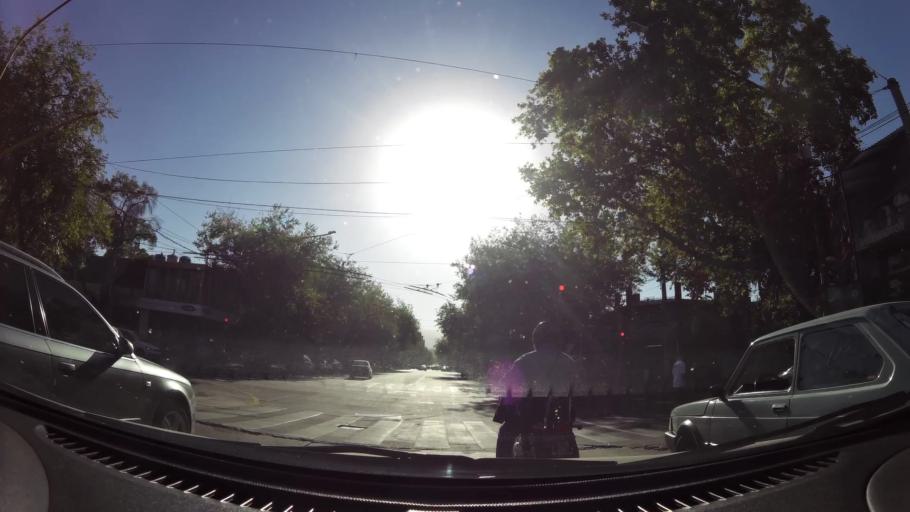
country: AR
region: Mendoza
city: Mendoza
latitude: -32.8961
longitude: -68.8347
